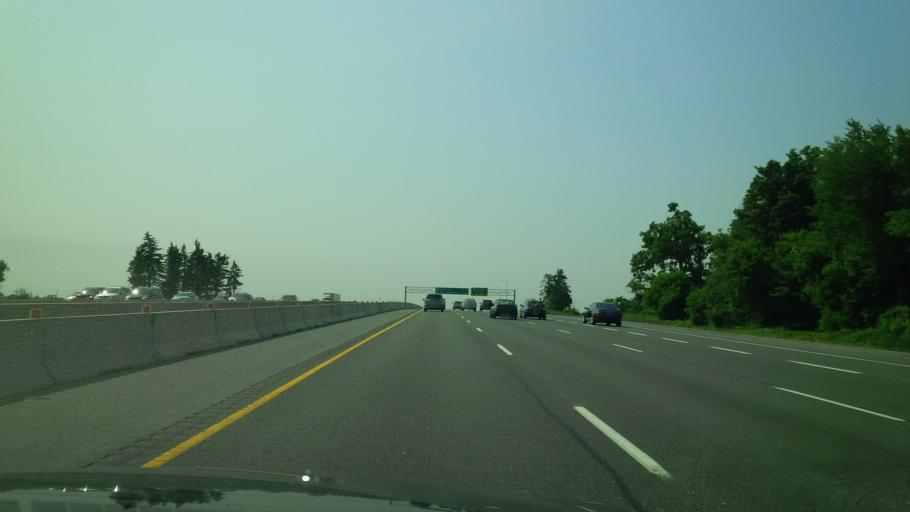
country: CA
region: Ontario
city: Vaughan
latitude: 43.9272
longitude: -79.5678
